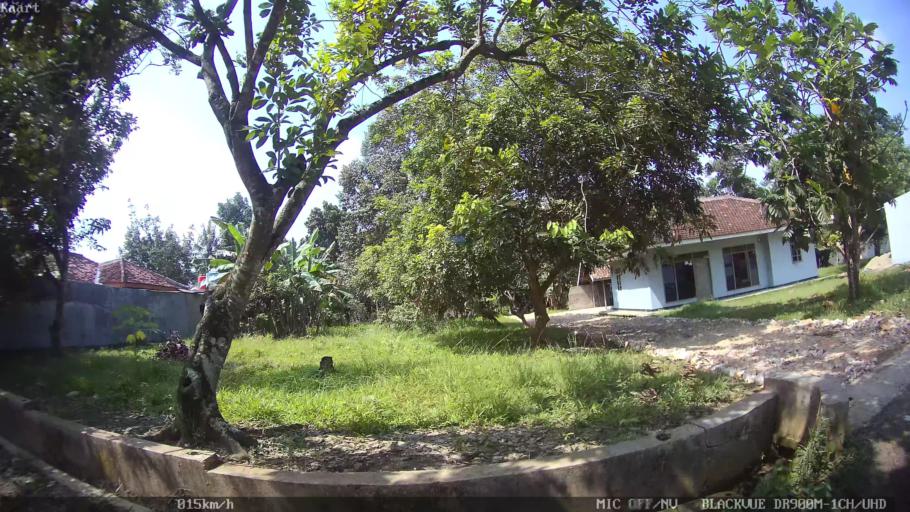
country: ID
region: Lampung
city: Kedaton
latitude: -5.3452
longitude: 105.2947
